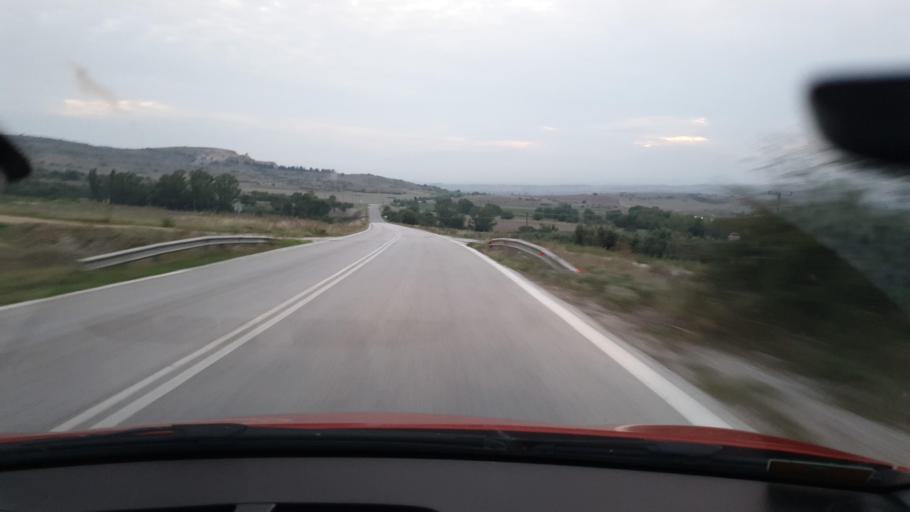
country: GR
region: Central Macedonia
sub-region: Nomos Kilkis
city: Polykastro
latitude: 41.0179
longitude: 22.6614
